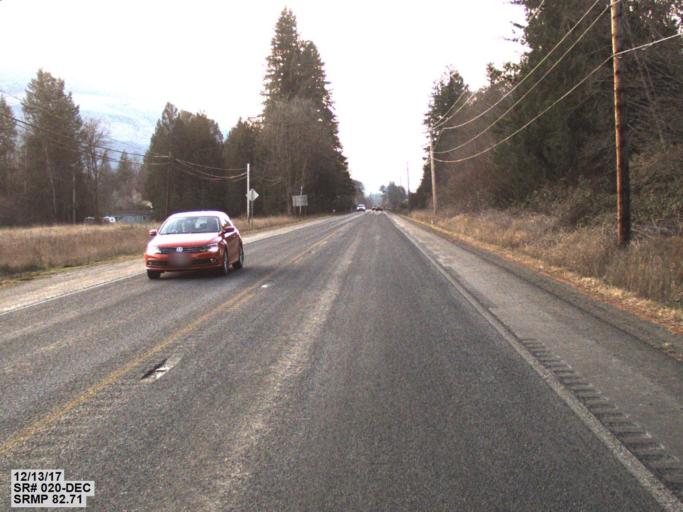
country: US
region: Washington
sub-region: Skagit County
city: Sedro-Woolley
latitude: 48.5339
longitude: -121.8787
